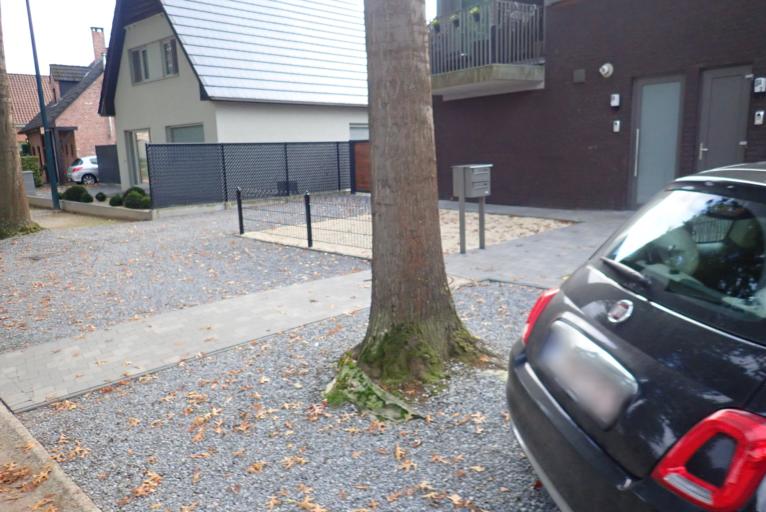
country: BE
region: Flanders
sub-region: Provincie Antwerpen
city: Vorselaar
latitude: 51.2072
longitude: 4.7690
